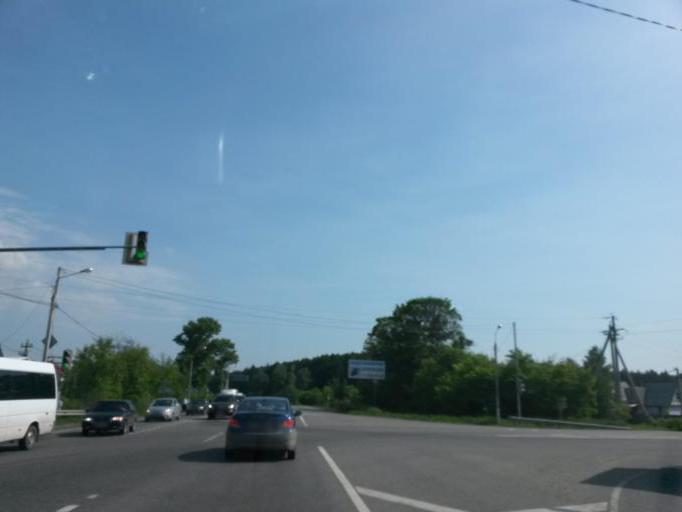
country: RU
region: Moskovskaya
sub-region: Chekhovskiy Rayon
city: Chekhov
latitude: 55.1881
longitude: 37.5001
